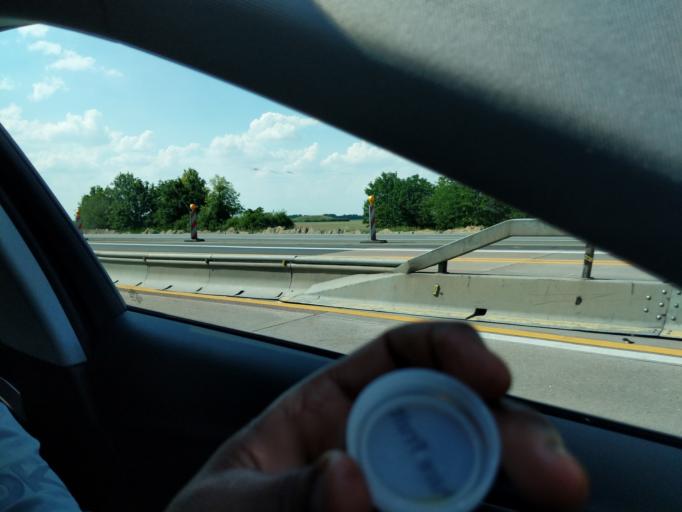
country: DE
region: Saxony
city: Rackwitz
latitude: 51.4143
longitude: 12.3333
